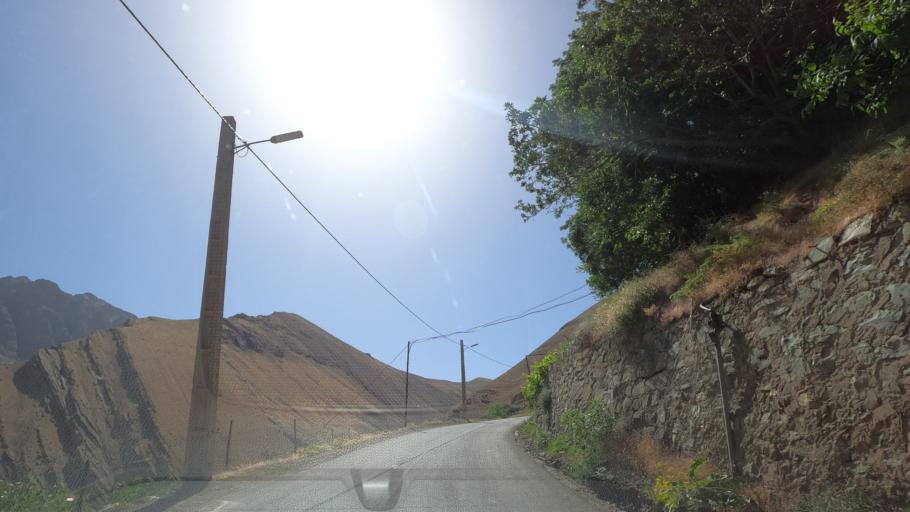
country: IR
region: Alborz
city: Karaj
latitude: 35.9424
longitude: 51.0827
